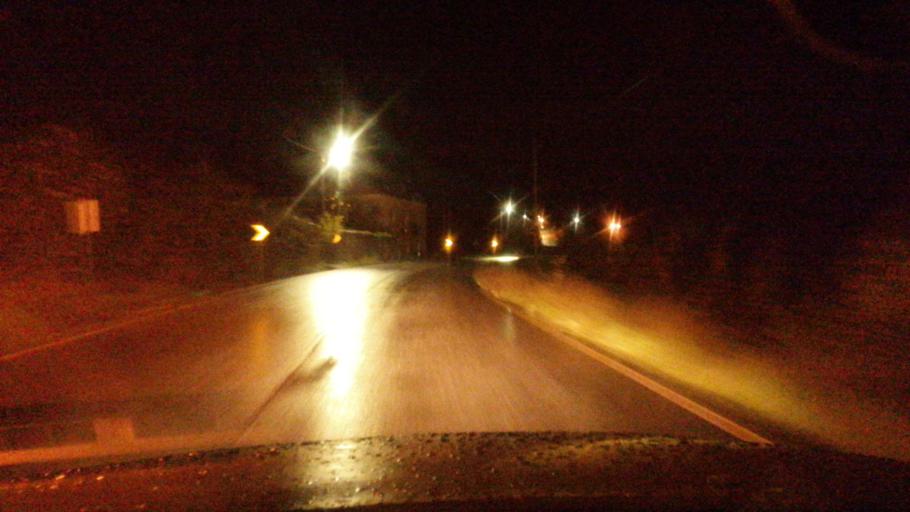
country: PT
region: Viseu
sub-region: Sernancelhe
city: Sernancelhe
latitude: 40.8927
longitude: -7.5169
